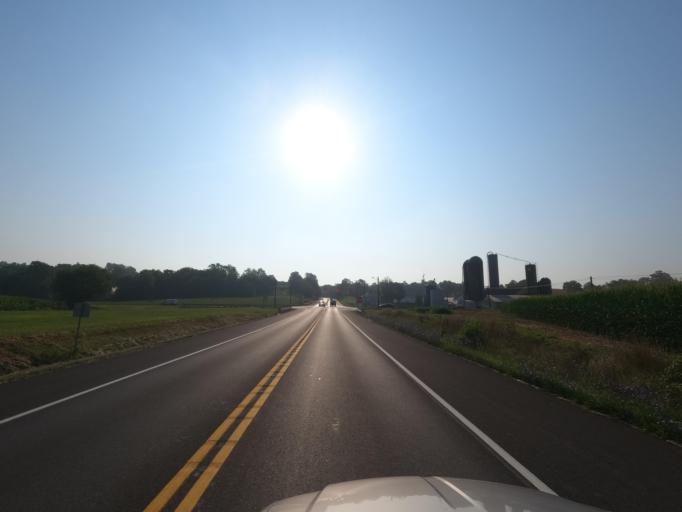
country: US
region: Pennsylvania
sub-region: Franklin County
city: Wayne Heights
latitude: 39.7079
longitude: -77.5740
